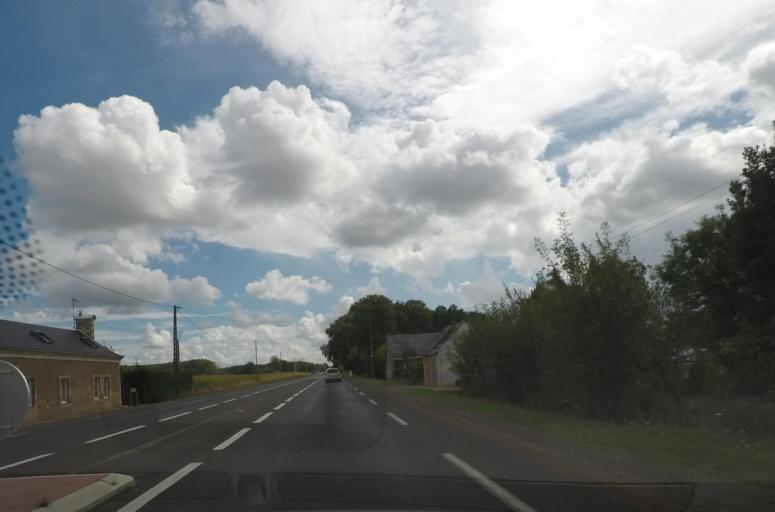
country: FR
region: Pays de la Loire
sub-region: Departement de la Sarthe
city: Bazouges-sur-le-Loir
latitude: 47.6909
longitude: -0.1537
